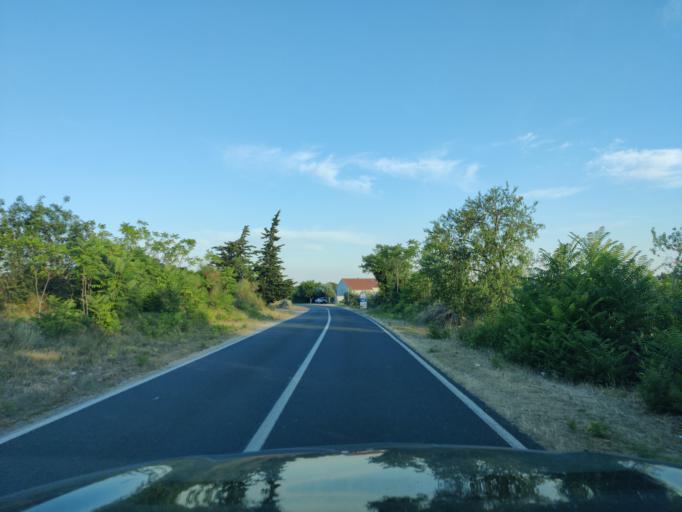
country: HR
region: Sibensko-Kniniska
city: Tribunj
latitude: 43.7703
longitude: 15.7277
